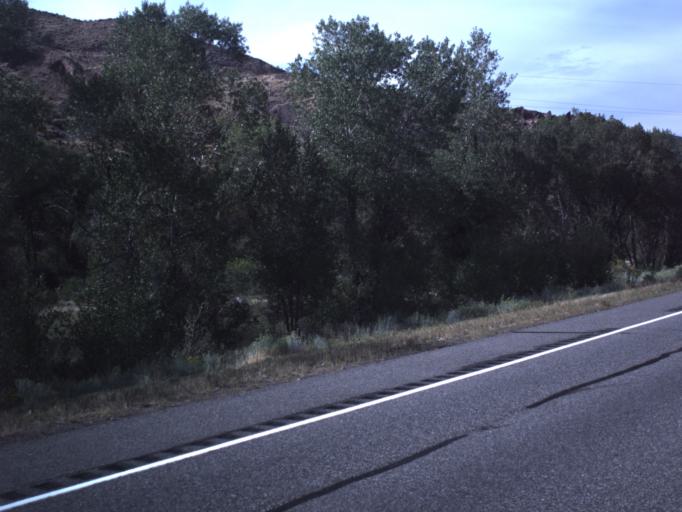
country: US
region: Utah
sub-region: Sevier County
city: Monroe
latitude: 38.5781
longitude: -112.2581
